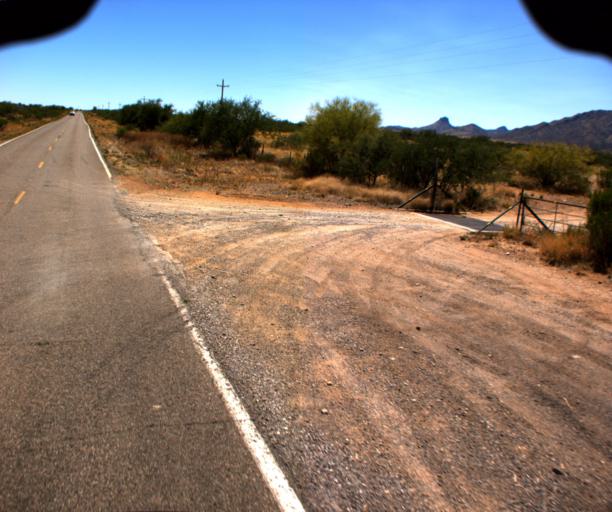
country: US
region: Arizona
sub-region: Pima County
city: Three Points
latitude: 31.7638
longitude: -111.4727
